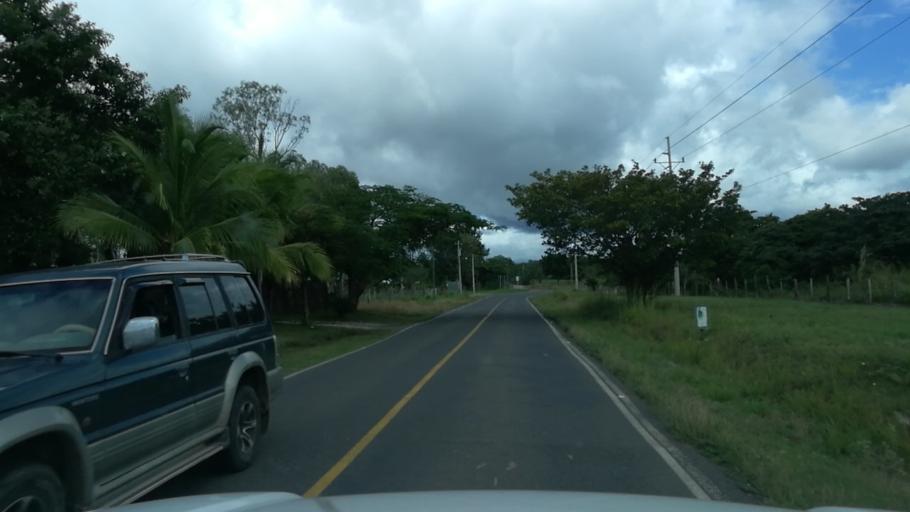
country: CR
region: Guanacaste
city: Bagaces
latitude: 10.5444
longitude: -85.2611
